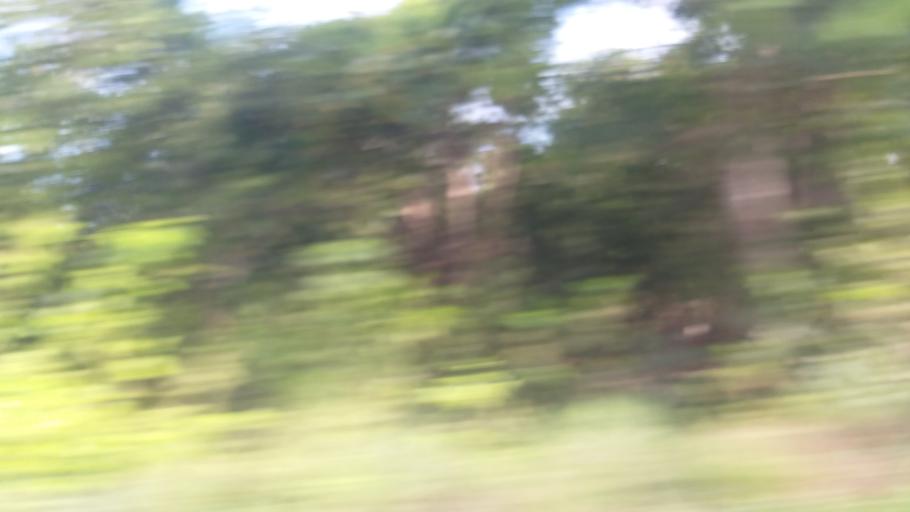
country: TH
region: Chaiyaphum
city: Ban Thaen
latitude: 16.3992
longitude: 102.3373
